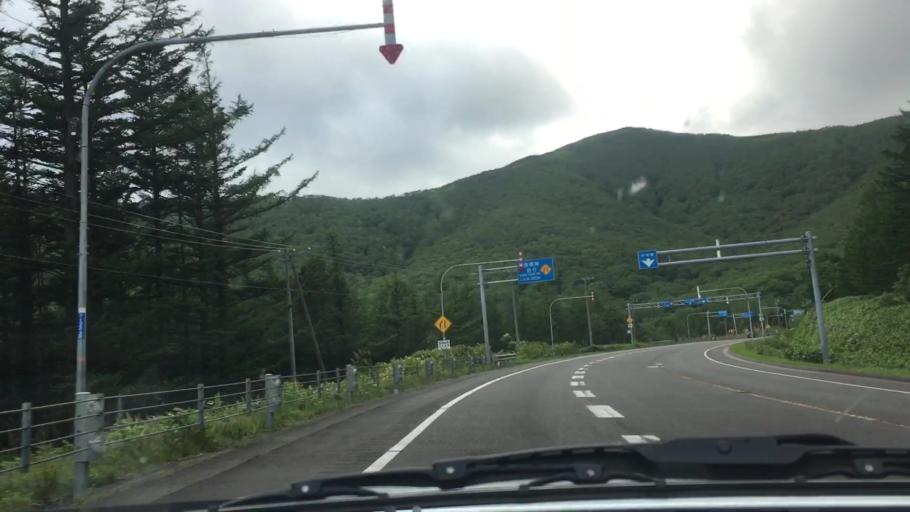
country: JP
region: Hokkaido
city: Shimo-furano
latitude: 43.1569
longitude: 142.7842
